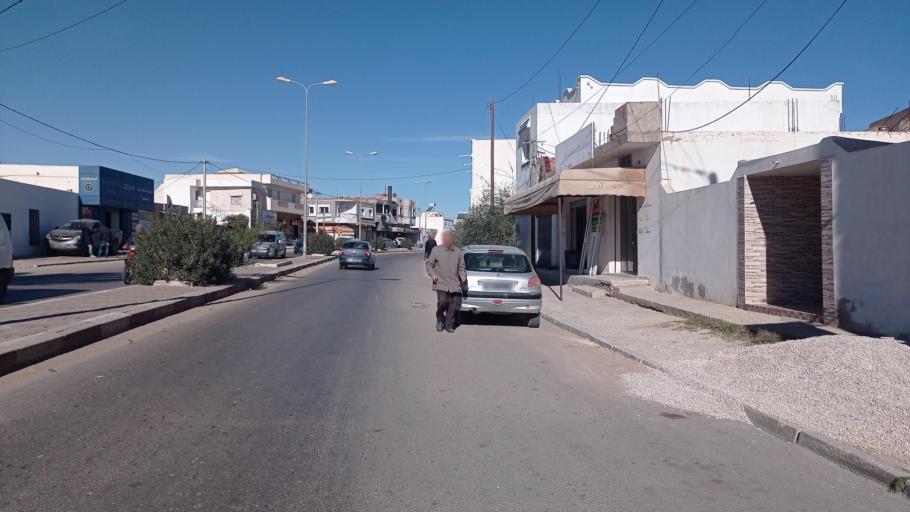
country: TN
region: Qabis
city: Gabes
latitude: 33.8409
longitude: 10.1145
